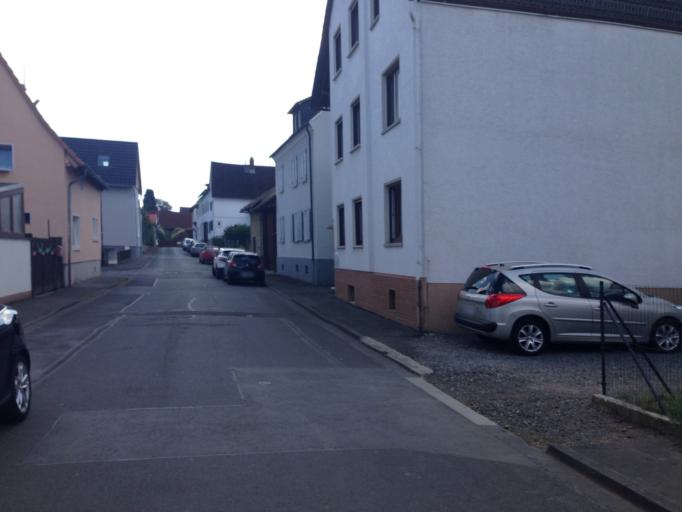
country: DE
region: Hesse
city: Allendorf an der Lahn
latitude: 50.5392
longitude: 8.6184
